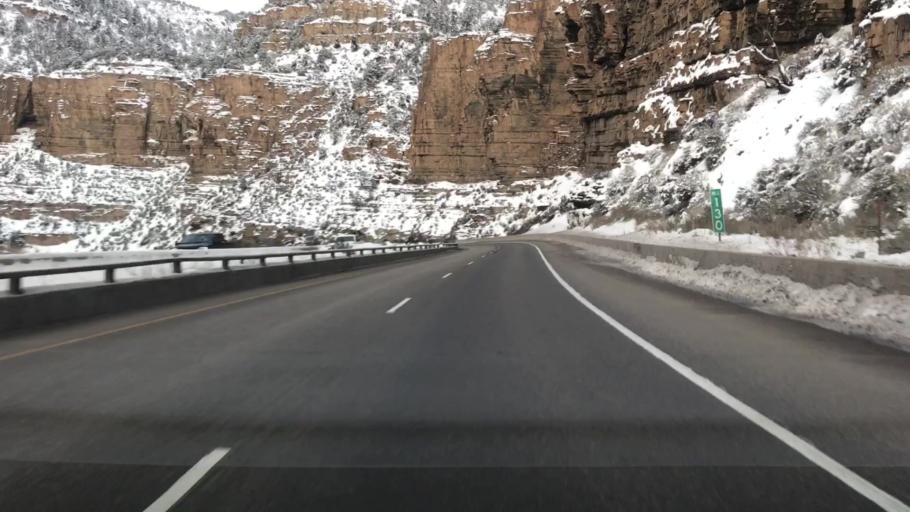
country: US
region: Colorado
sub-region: Eagle County
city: Gypsum
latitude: 39.6244
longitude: -107.1182
